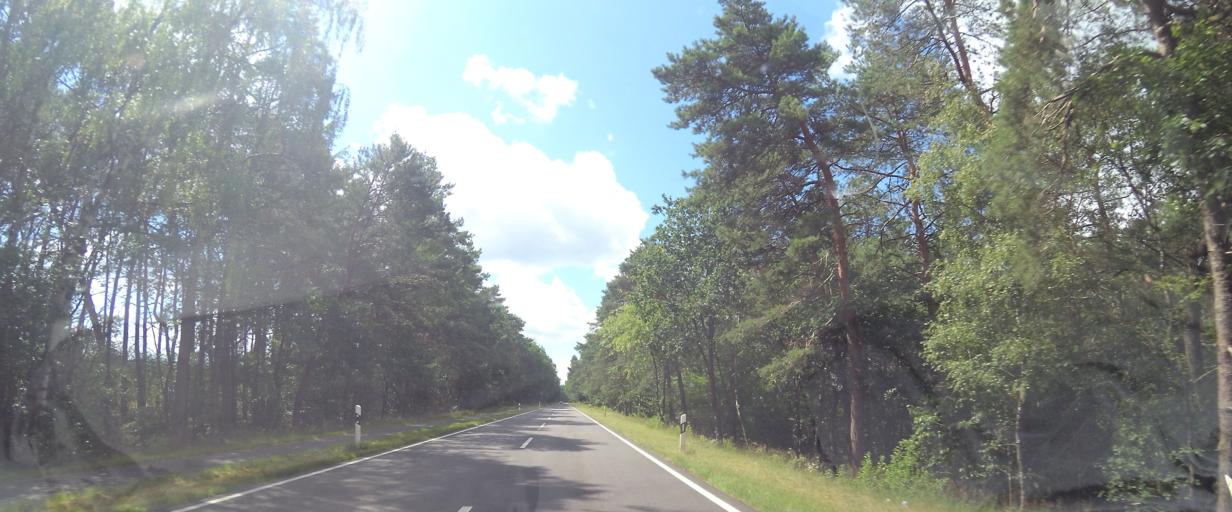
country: DE
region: Lower Saxony
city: Niederlangen
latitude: 52.8006
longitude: 7.3096
